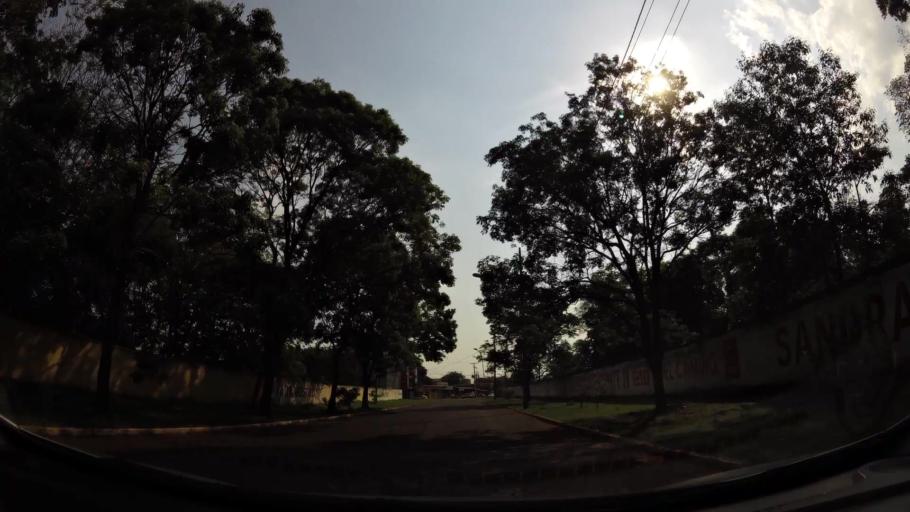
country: PY
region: Alto Parana
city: Presidente Franco
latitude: -25.5248
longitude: -54.6161
